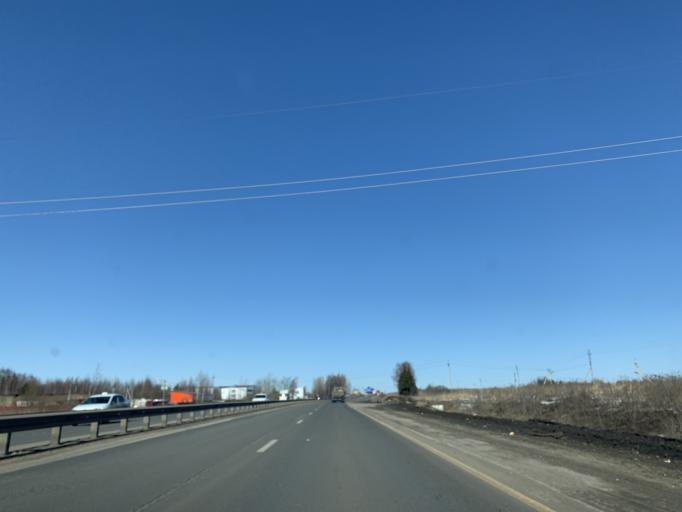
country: RU
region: Jaroslavl
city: Konstantinovskiy
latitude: 57.8430
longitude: 39.5507
